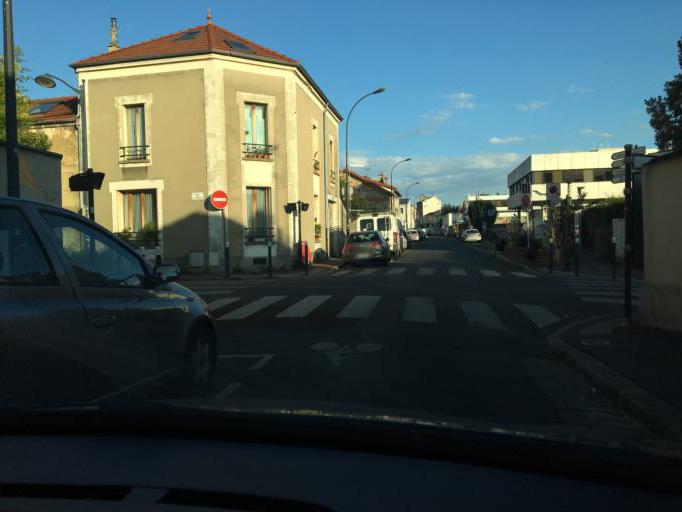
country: FR
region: Ile-de-France
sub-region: Departement du Val-de-Marne
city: Fontenay-sous-Bois
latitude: 48.8501
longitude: 2.4739
